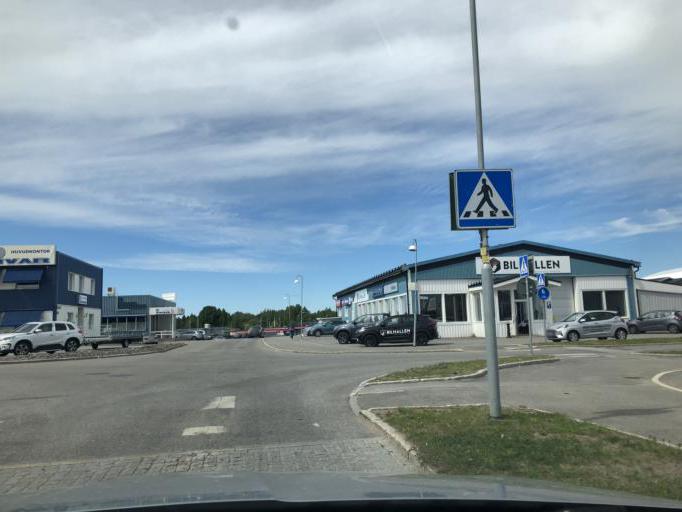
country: SE
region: Norrbotten
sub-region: Pitea Kommun
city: Pitea
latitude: 65.3229
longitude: 21.4432
